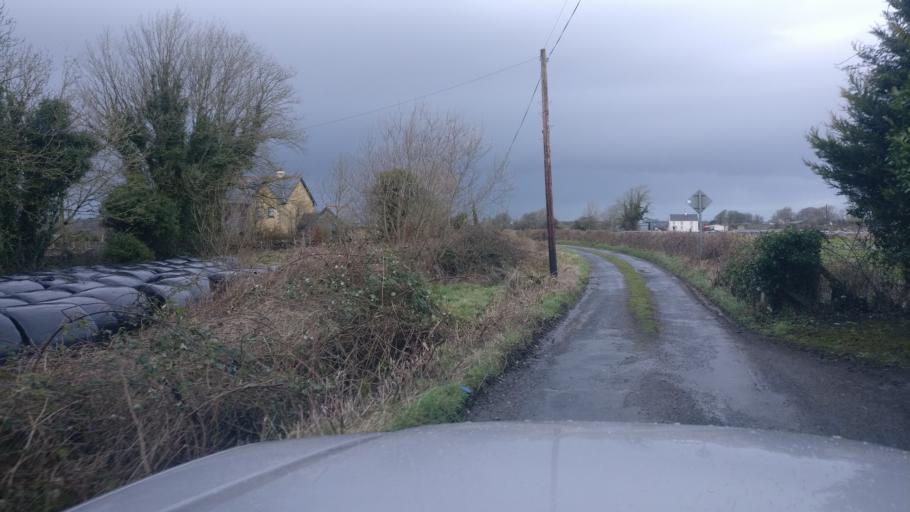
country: IE
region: Connaught
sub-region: County Galway
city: Loughrea
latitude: 53.1996
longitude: -8.6131
